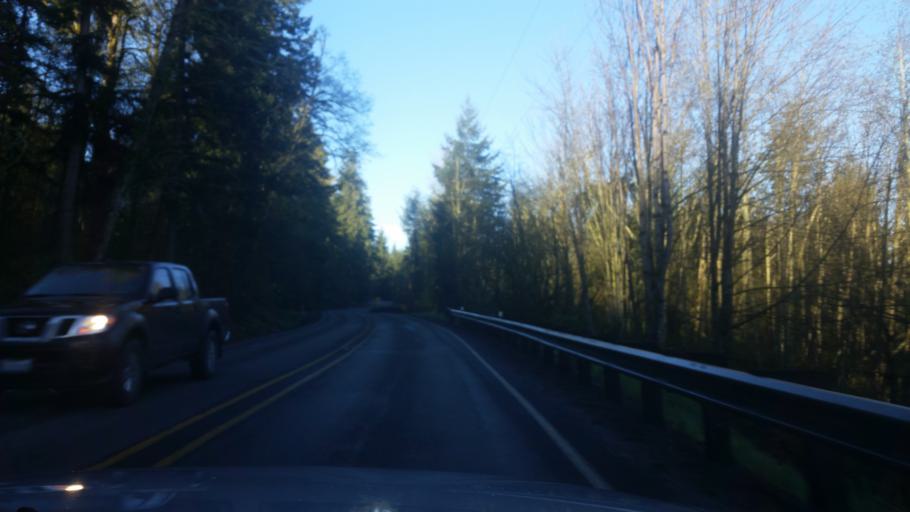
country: US
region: Washington
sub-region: Pierce County
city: Eatonville
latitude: 46.8560
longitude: -122.2598
